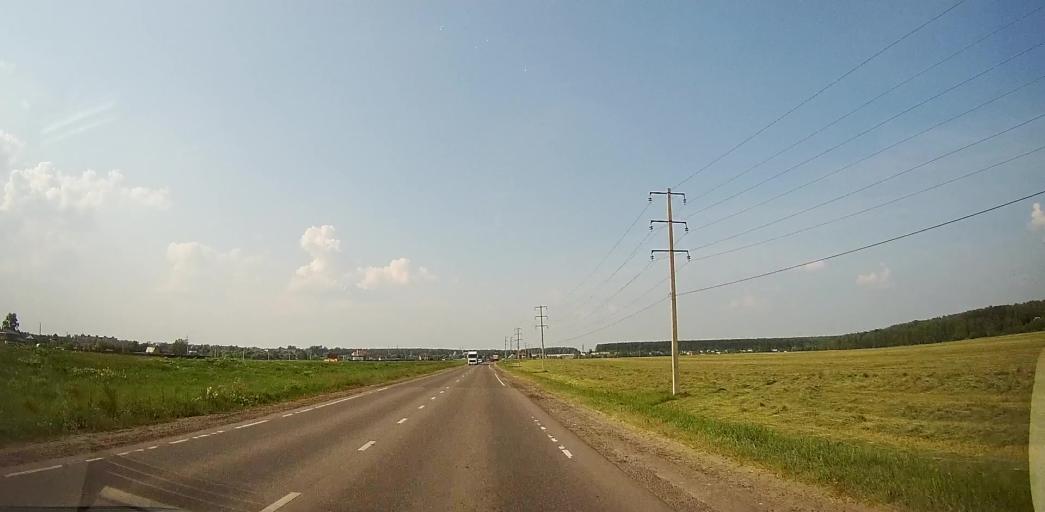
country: RU
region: Moskovskaya
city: Barybino
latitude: 55.2659
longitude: 37.9163
